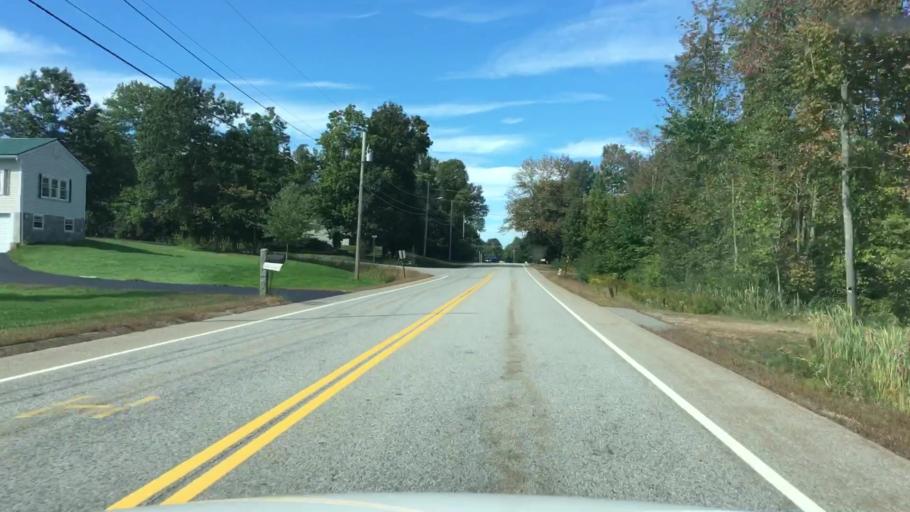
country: US
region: Maine
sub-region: Cumberland County
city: Gorham
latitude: 43.6694
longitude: -70.4086
